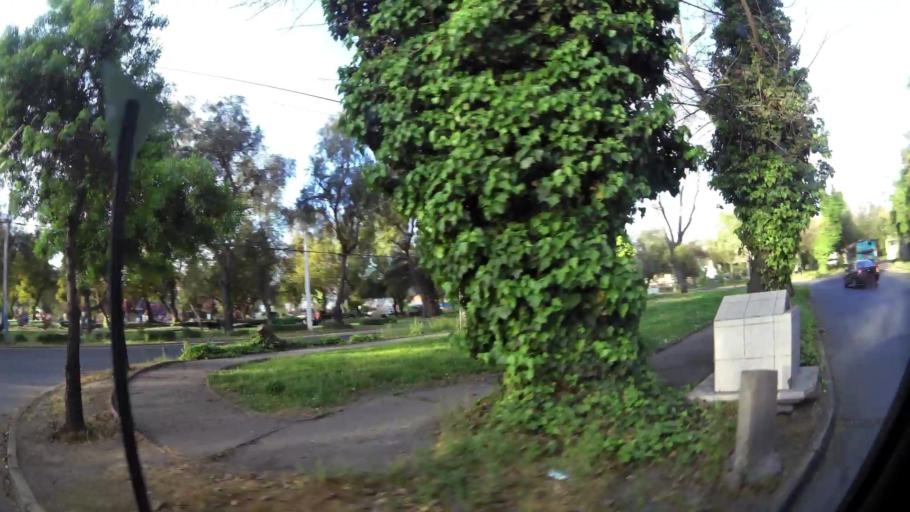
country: CL
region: Santiago Metropolitan
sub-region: Provincia de Santiago
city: Lo Prado
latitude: -33.4558
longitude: -70.7222
